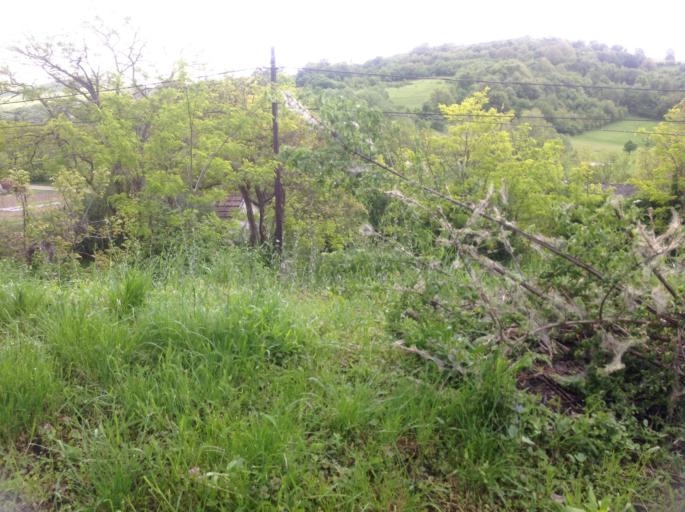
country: HU
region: Komarom-Esztergom
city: Kesztolc
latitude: 47.7142
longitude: 18.8088
